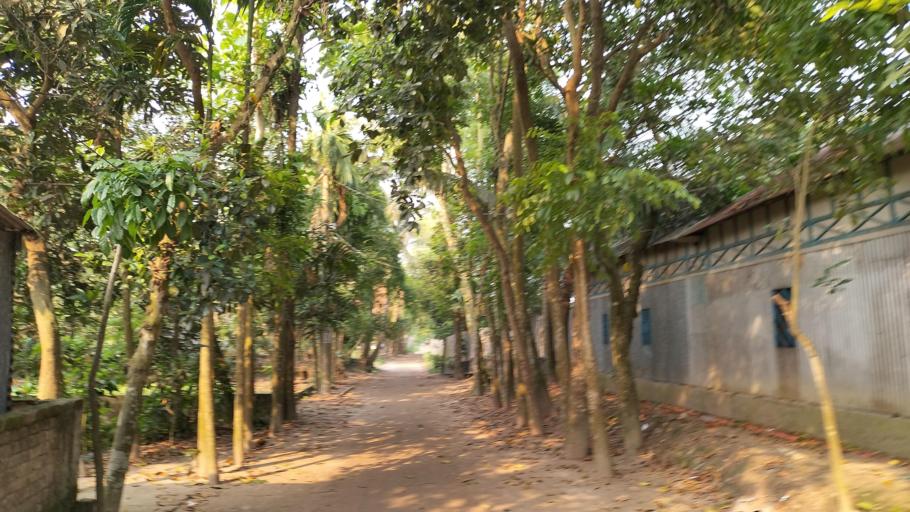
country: BD
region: Dhaka
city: Azimpur
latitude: 23.6676
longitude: 90.3172
